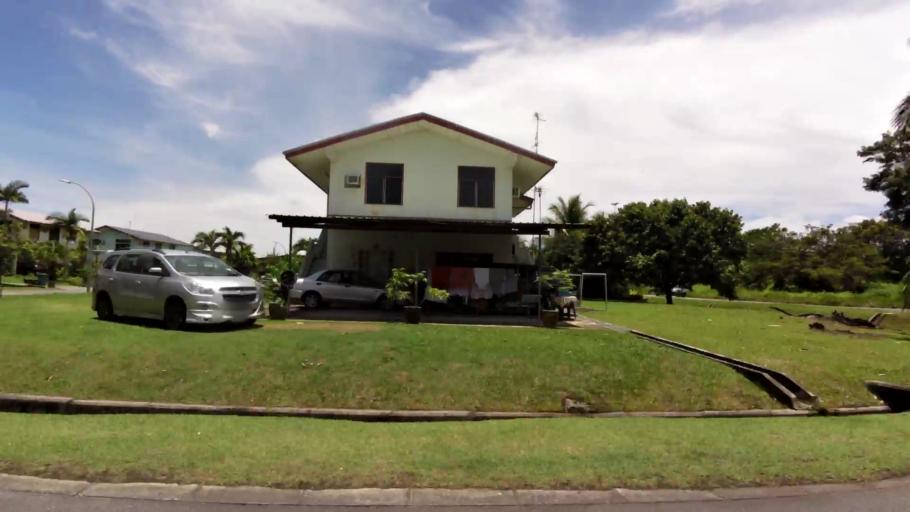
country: BN
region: Belait
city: Kuala Belait
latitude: 4.5843
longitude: 114.2346
